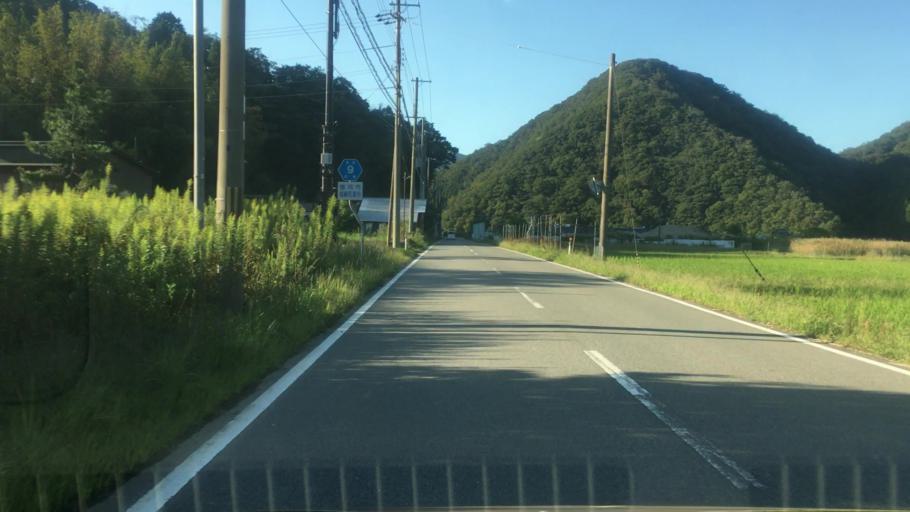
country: JP
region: Hyogo
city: Toyooka
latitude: 35.6132
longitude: 134.8277
